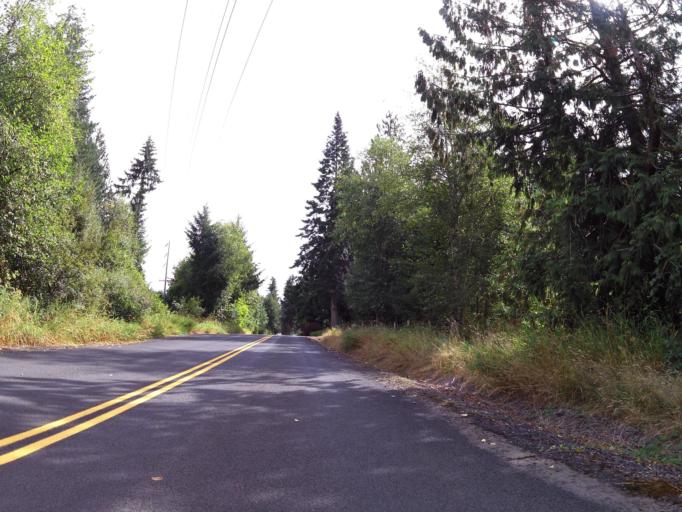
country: US
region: Washington
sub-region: Cowlitz County
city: Castle Rock
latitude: 46.3148
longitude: -122.9248
